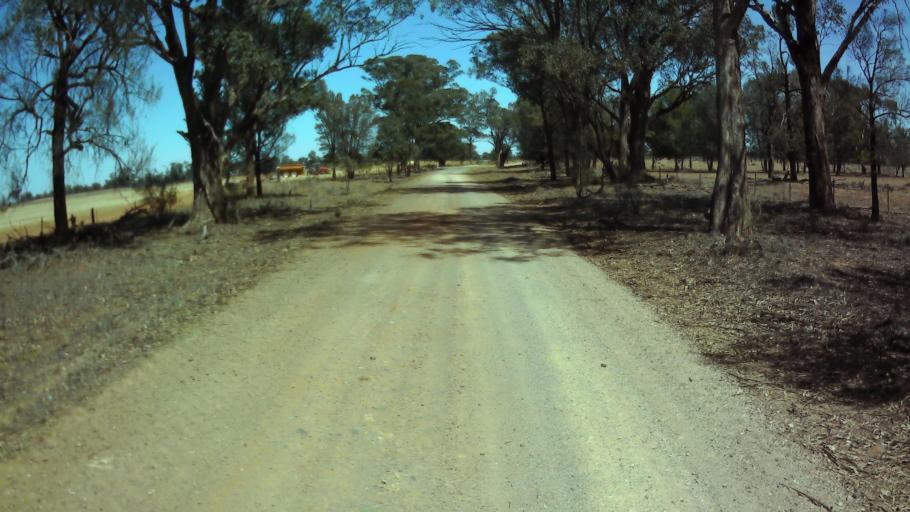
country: AU
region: New South Wales
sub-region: Weddin
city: Grenfell
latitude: -34.0678
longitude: 147.8878
